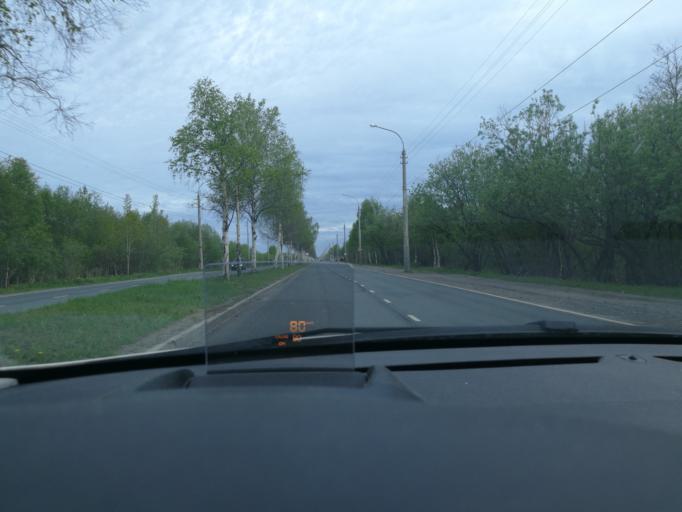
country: RU
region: Arkhangelskaya
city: Arkhangel'sk
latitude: 64.6096
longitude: 40.5247
